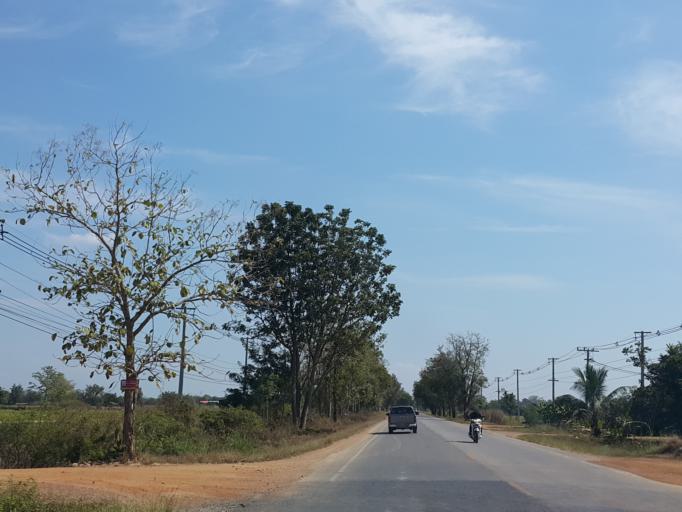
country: TH
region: Sukhothai
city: Sawankhalok
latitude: 17.3087
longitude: 99.7384
